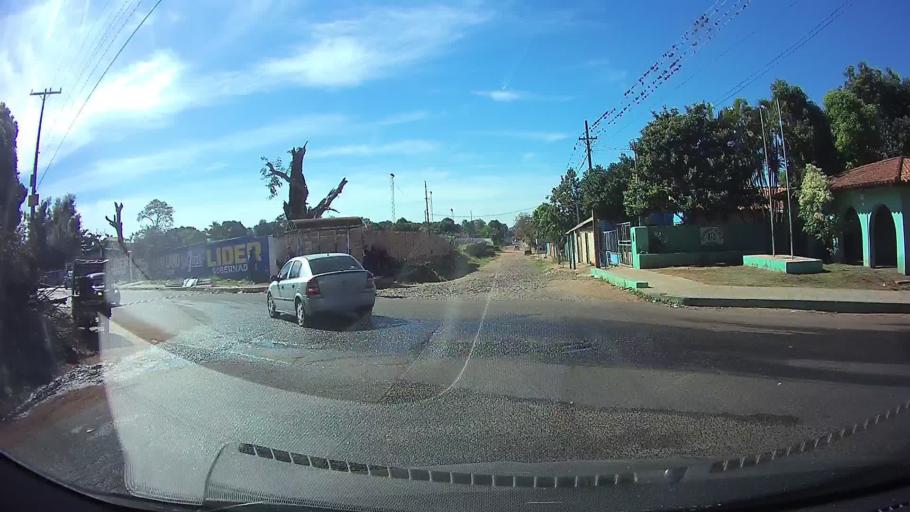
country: PY
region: Central
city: Villa Elisa
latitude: -25.3758
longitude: -57.5792
